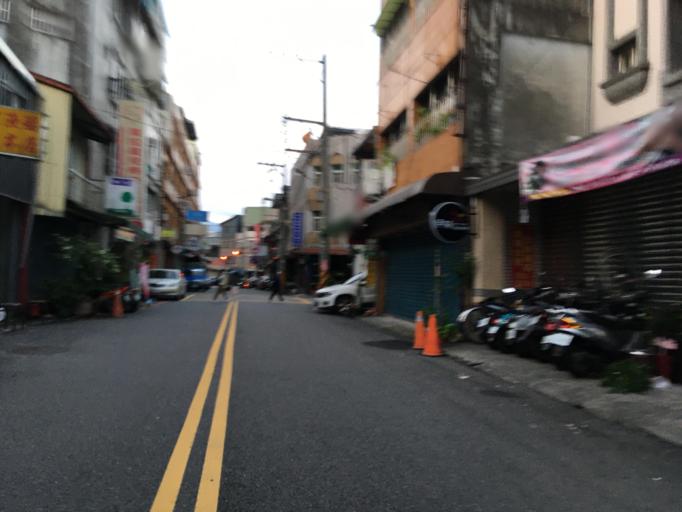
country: TW
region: Taiwan
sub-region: Yilan
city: Yilan
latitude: 24.6737
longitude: 121.7683
